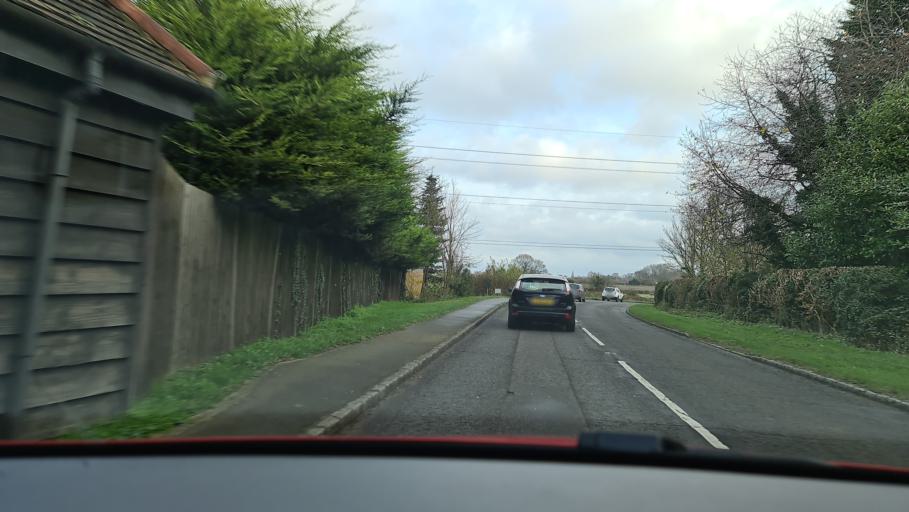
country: GB
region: England
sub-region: Buckinghamshire
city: Weston Turville
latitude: 51.7685
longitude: -0.7801
